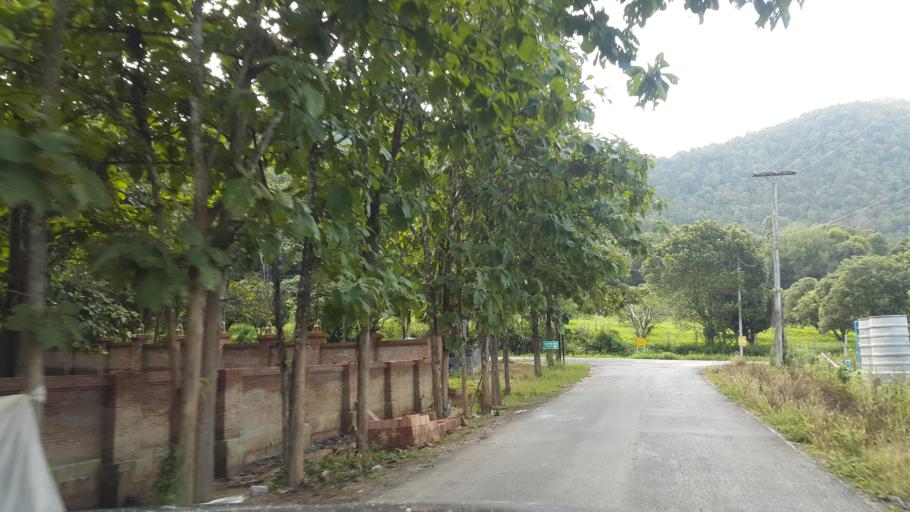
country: TH
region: Chiang Mai
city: Mae On
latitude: 18.7191
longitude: 99.2266
